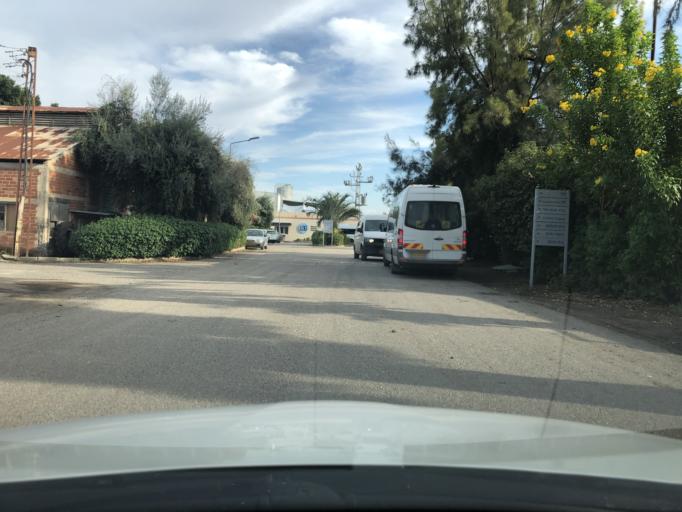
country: IL
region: Northern District
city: Yavne'el
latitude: 32.6570
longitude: 35.5812
